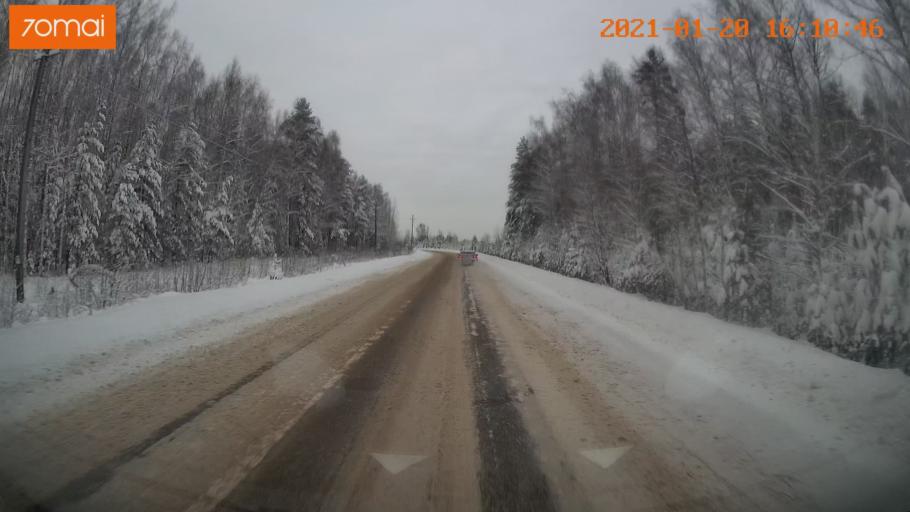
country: RU
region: Vladimir
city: Sudogda
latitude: 56.0952
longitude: 40.7859
